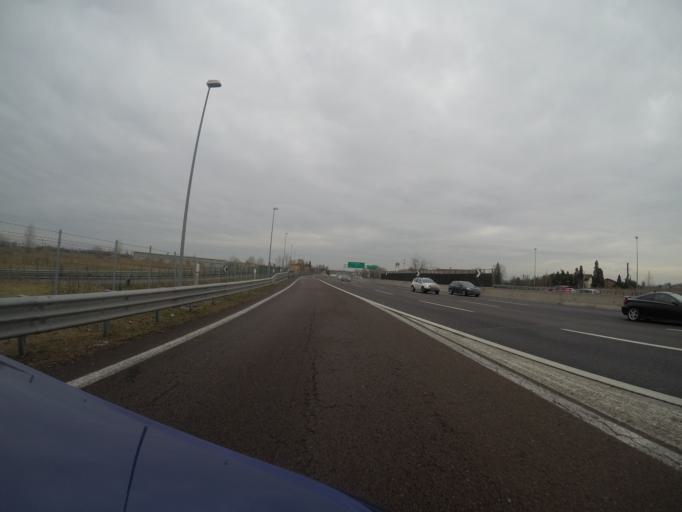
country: IT
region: Emilia-Romagna
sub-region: Provincia di Modena
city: Campogalliano
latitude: 44.6607
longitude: 10.8587
